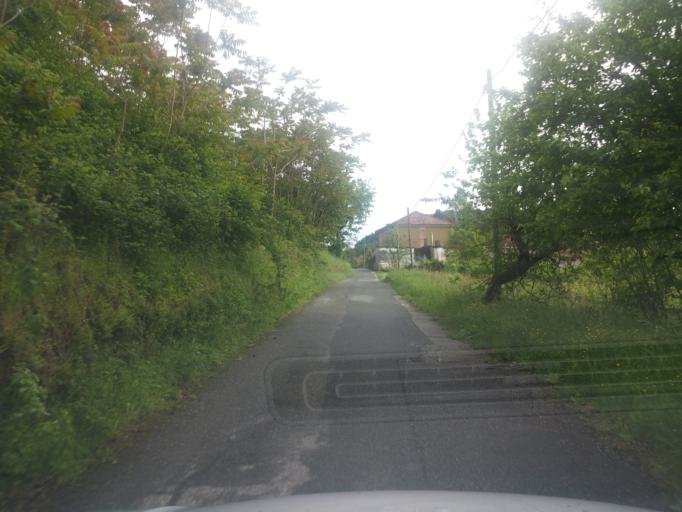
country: IT
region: Piedmont
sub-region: Provincia di Torino
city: Cossano Canavese
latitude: 45.3874
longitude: 8.0081
